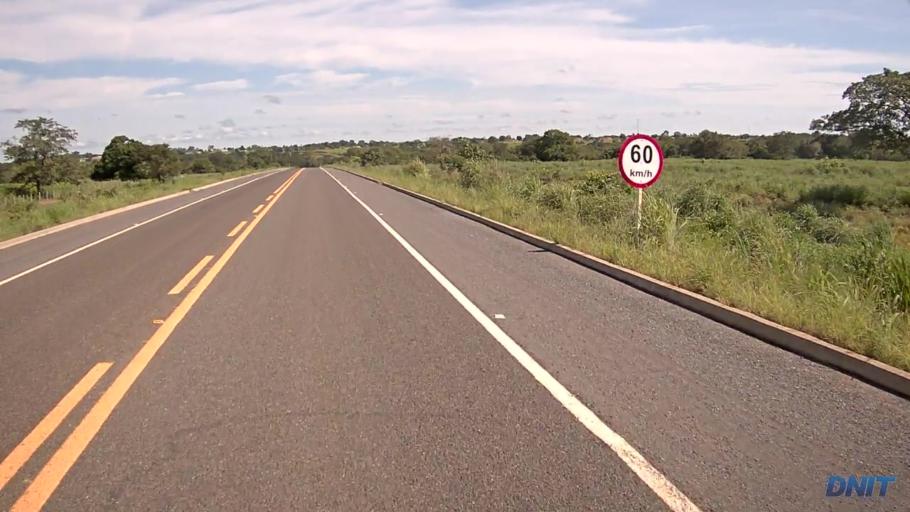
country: BR
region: Goias
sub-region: Sao Miguel Do Araguaia
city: Sao Miguel do Araguaia
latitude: -13.3036
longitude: -50.1740
